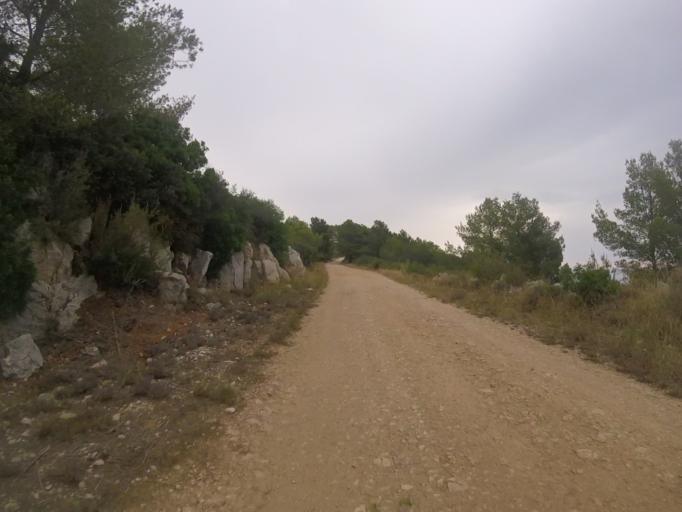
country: ES
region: Valencia
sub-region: Provincia de Castello
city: Alcoceber
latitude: 40.2731
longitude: 0.2781
